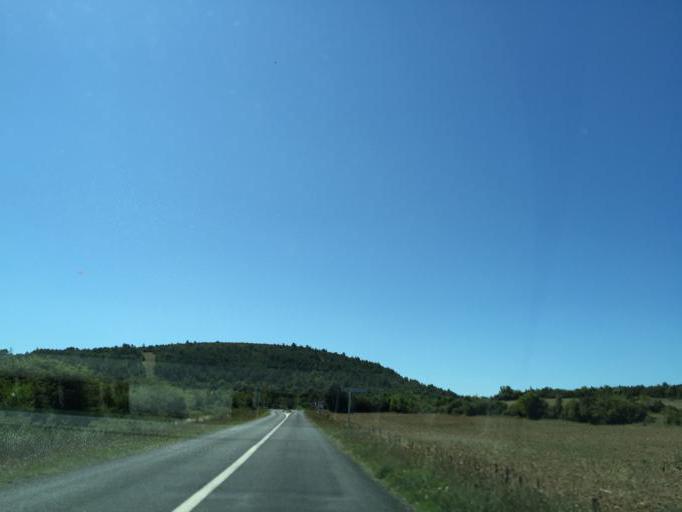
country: FR
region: Midi-Pyrenees
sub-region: Departement de l'Aveyron
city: La Cavalerie
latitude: 43.9115
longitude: 3.3108
